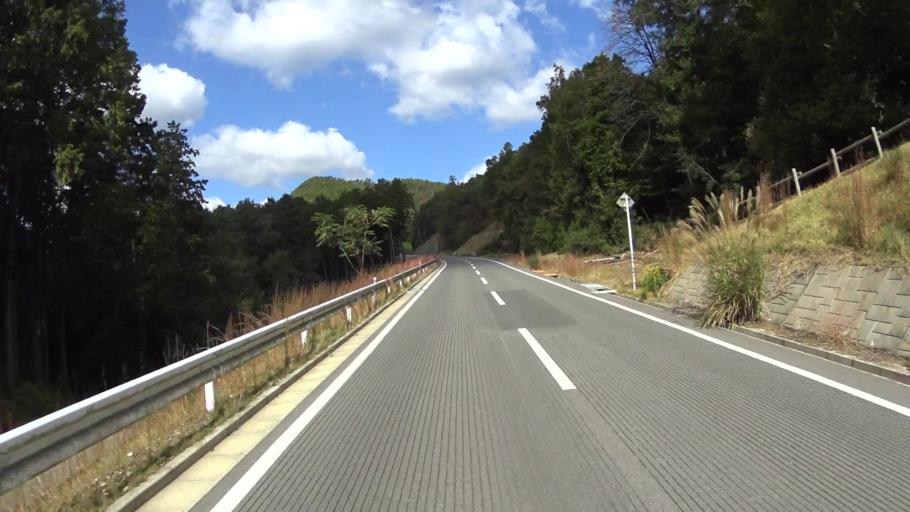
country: JP
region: Kyoto
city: Kameoka
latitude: 35.0962
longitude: 135.5515
